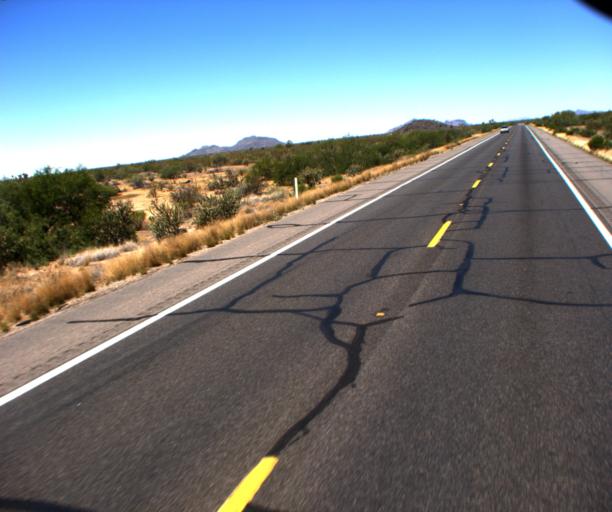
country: US
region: Arizona
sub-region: Yavapai County
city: Congress
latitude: 34.1637
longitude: -113.0085
